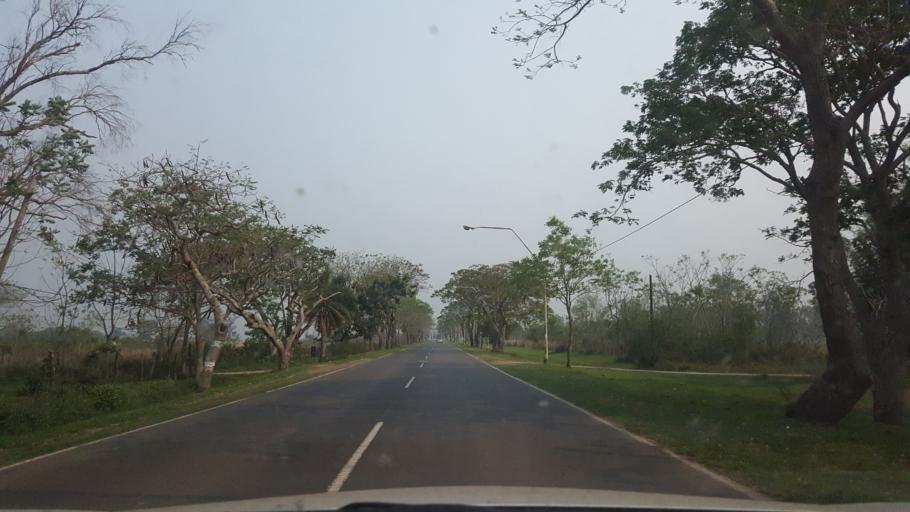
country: AR
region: Corrientes
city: Ita Ibate
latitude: -27.4369
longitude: -57.3396
